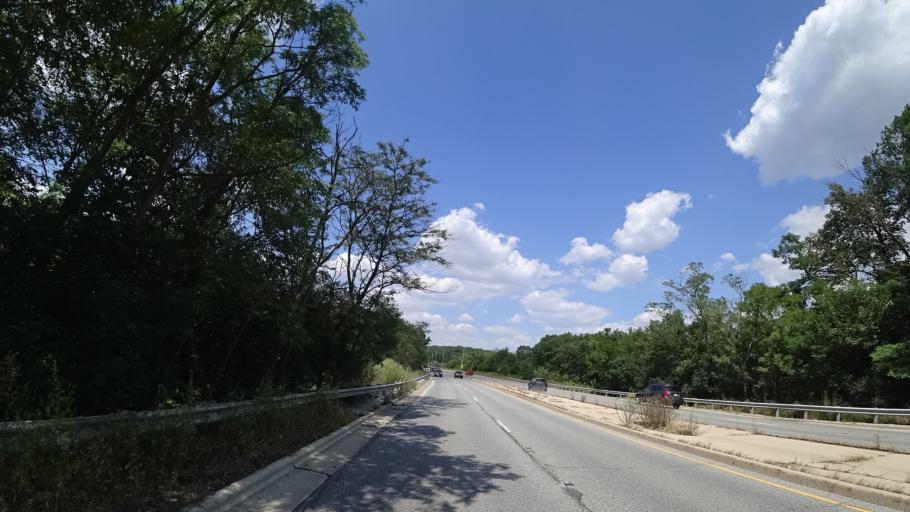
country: US
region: Illinois
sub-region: Cook County
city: Palos Heights
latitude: 41.6286
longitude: -87.7955
